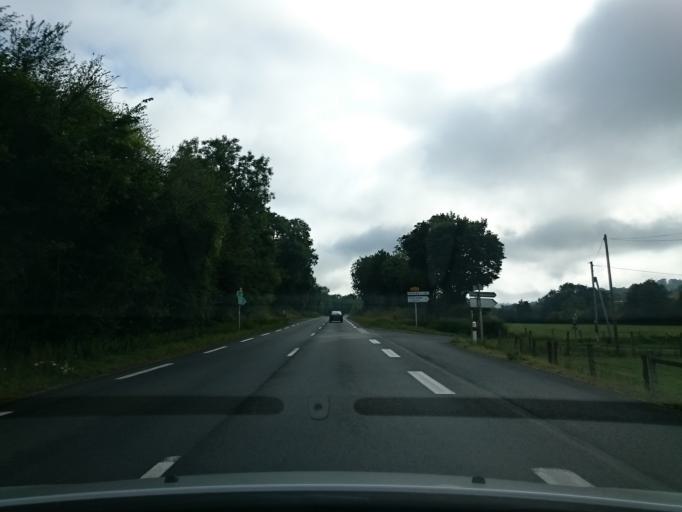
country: FR
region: Lower Normandy
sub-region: Departement du Calvados
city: Cambremer
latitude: 49.1207
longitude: 0.0681
